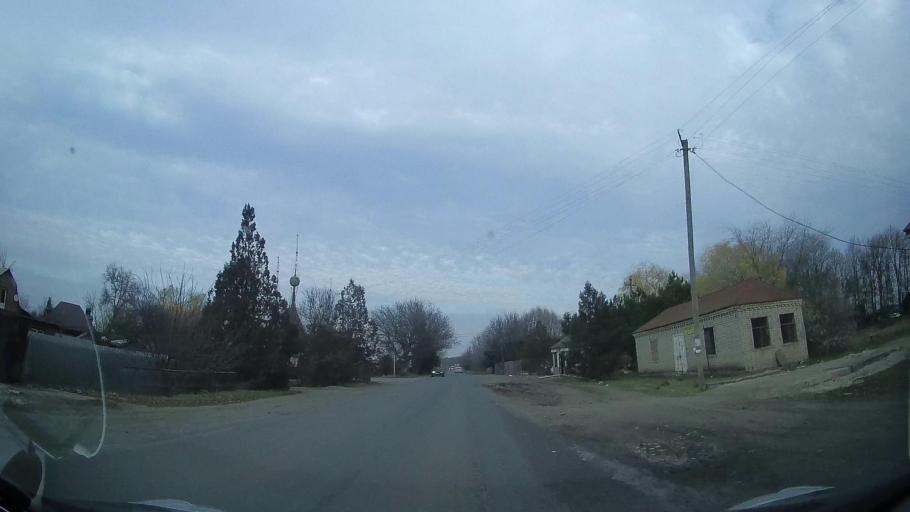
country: RU
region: Rostov
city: Ol'ginskaya
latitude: 47.1320
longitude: 39.8856
